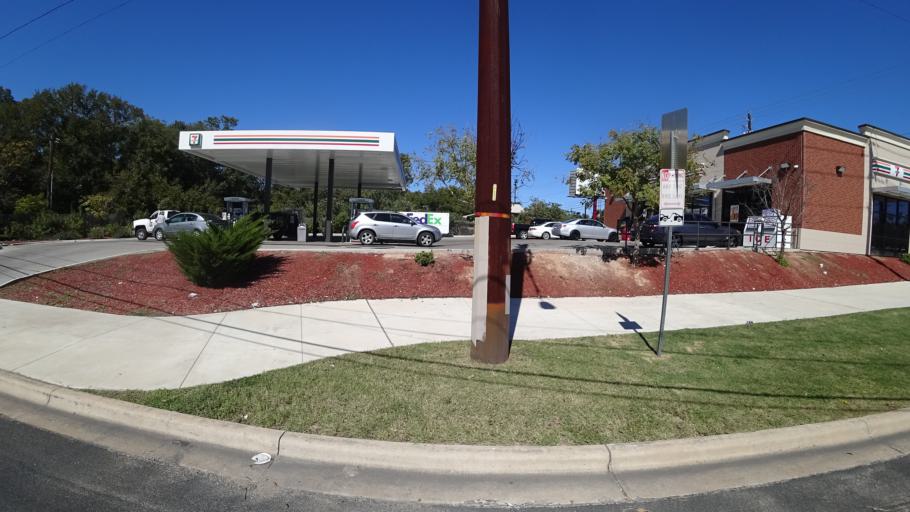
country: US
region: Texas
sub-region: Travis County
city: Austin
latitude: 30.2892
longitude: -97.7078
